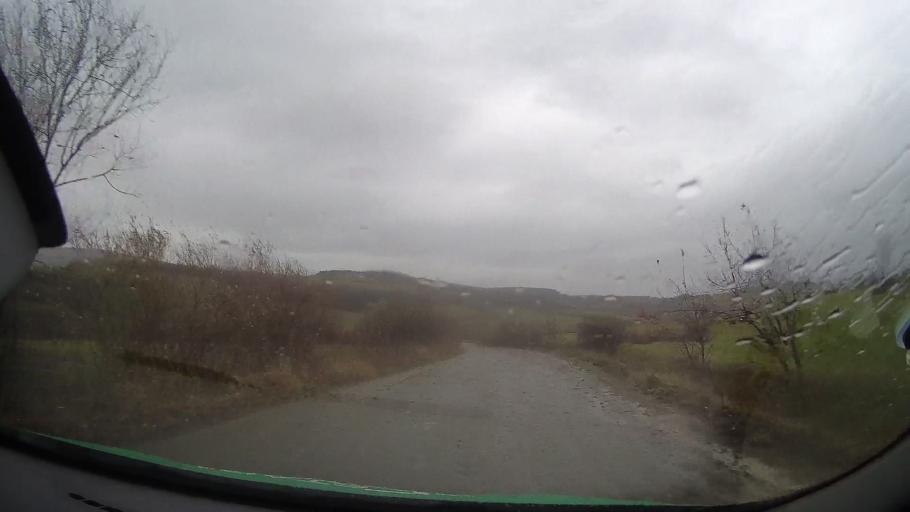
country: RO
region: Bistrita-Nasaud
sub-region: Comuna Monor
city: Monor
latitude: 46.9488
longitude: 24.7133
